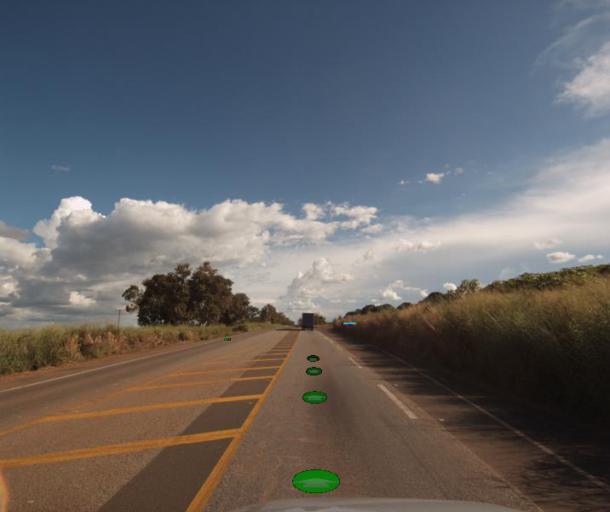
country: BR
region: Goias
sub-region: Porangatu
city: Porangatu
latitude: -13.1013
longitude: -49.1984
